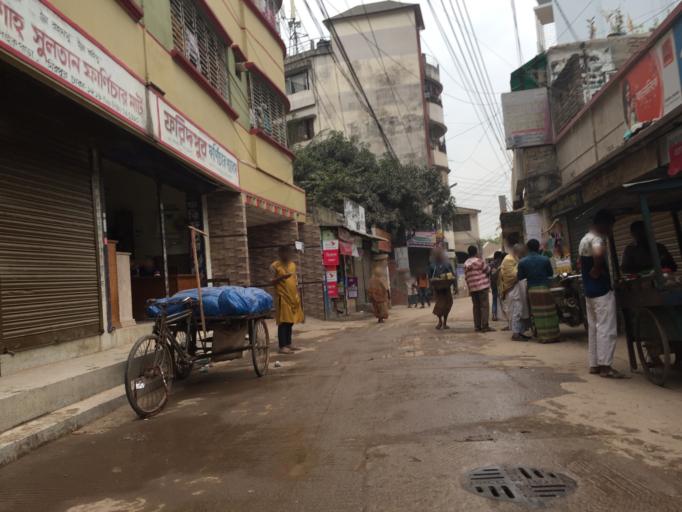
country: BD
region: Dhaka
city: Azimpur
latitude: 23.7891
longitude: 90.3598
